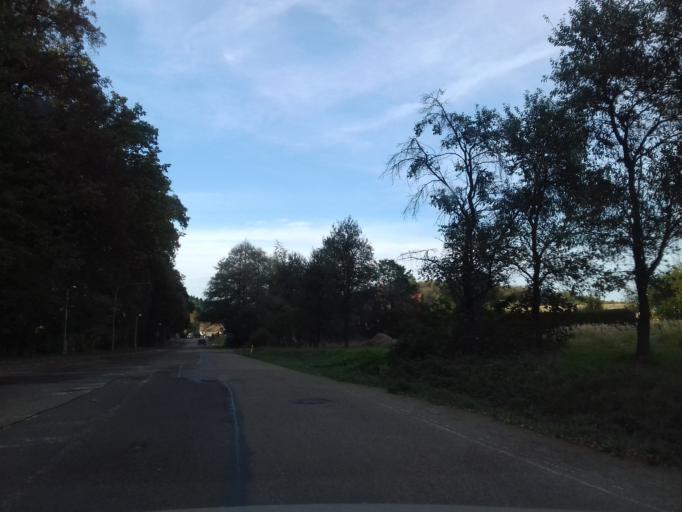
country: CZ
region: Central Bohemia
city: Neveklov
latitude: 49.7566
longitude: 14.5295
